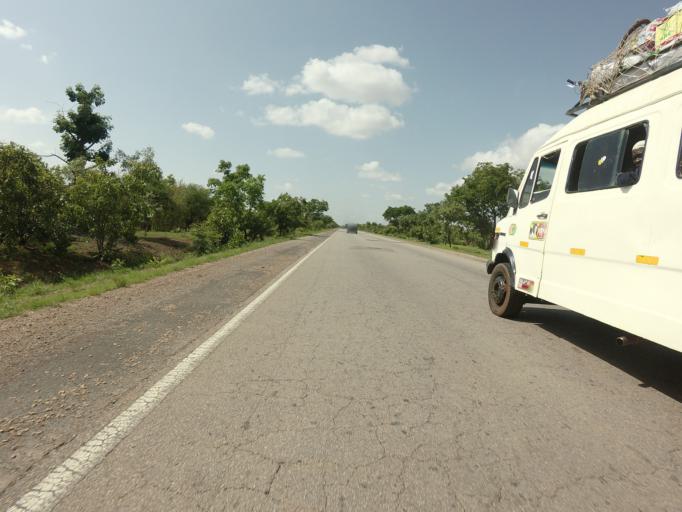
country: GH
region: Northern
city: Savelugu
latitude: 9.9472
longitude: -0.8381
